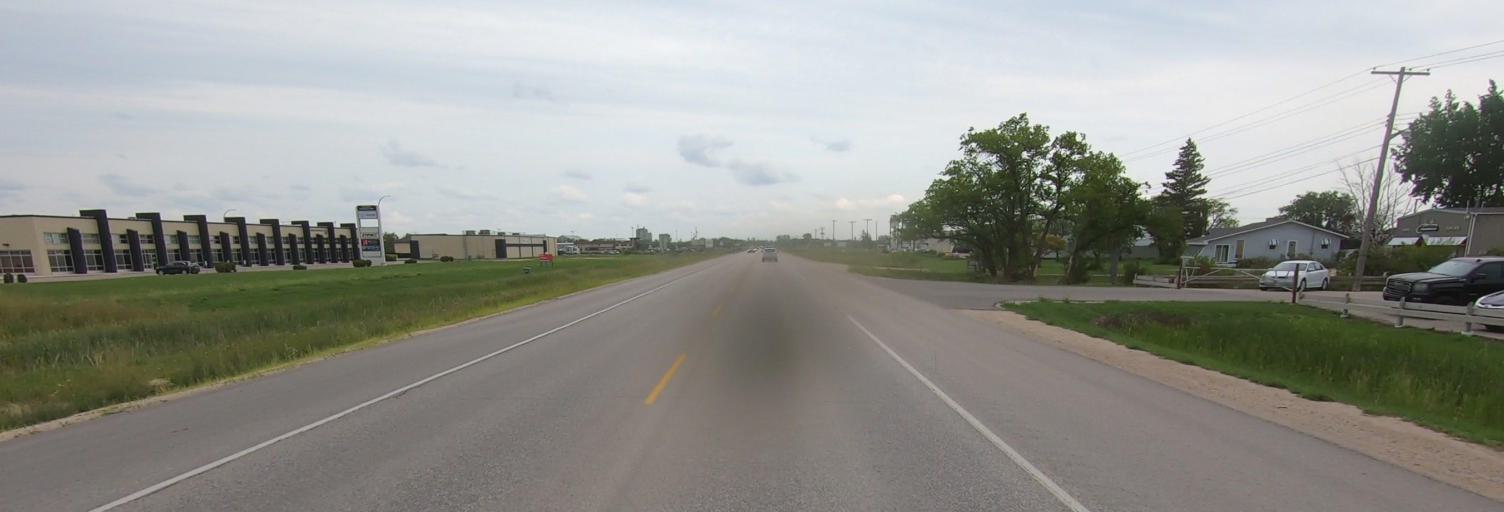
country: CA
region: Manitoba
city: Winnipeg
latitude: 49.8092
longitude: -97.2341
